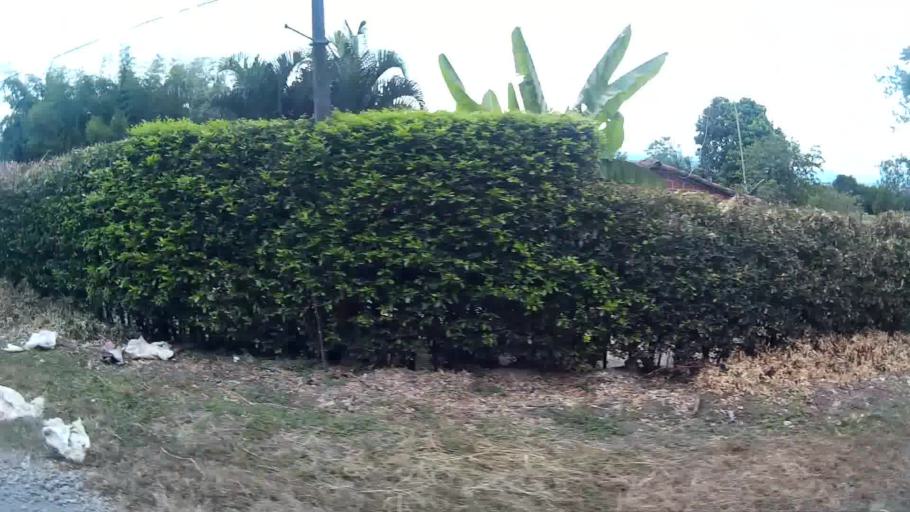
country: CO
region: Risaralda
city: La Virginia
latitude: 4.9156
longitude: -75.8682
